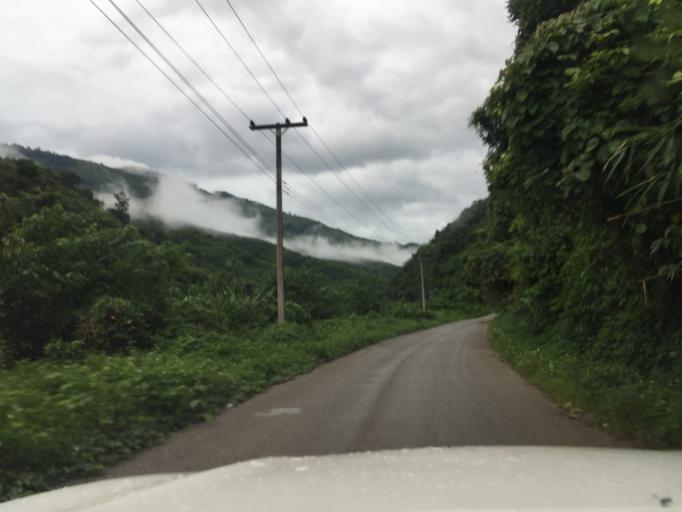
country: LA
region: Oudomxai
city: Muang La
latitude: 21.0116
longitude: 102.2336
